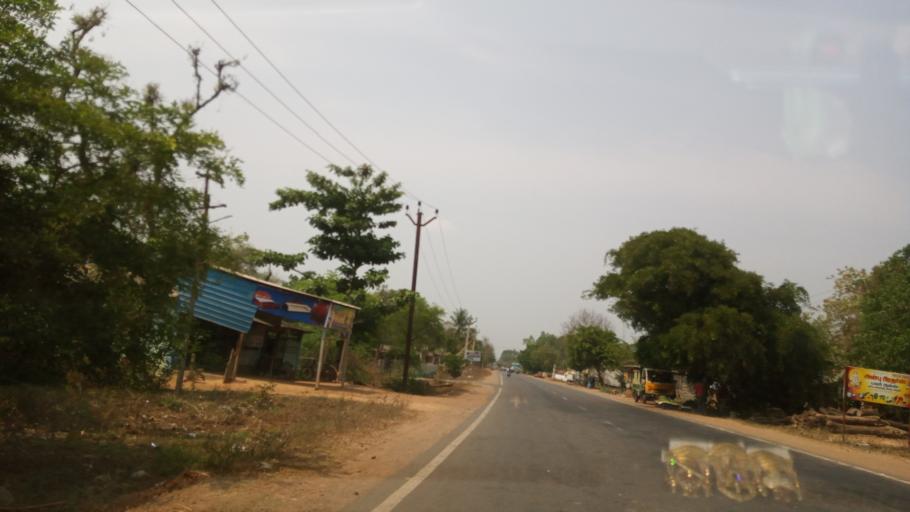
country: IN
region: Tamil Nadu
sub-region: Ariyalur
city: Jayamkondacholapuram
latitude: 11.2222
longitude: 79.3685
